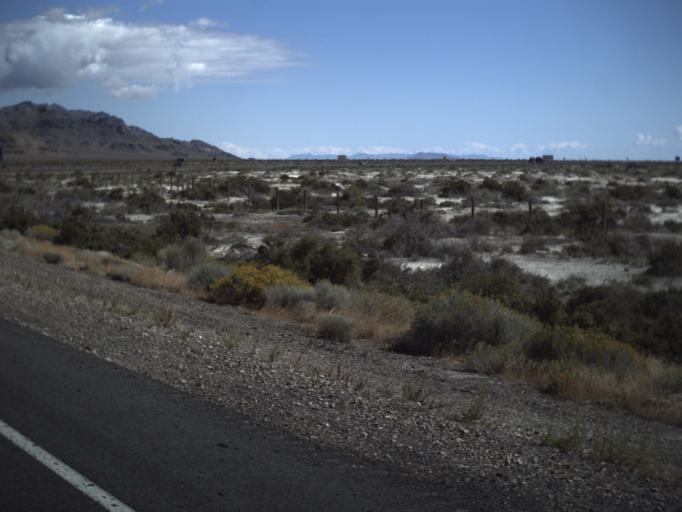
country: US
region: Utah
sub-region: Tooele County
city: Wendover
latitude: 40.7437
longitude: -114.0178
